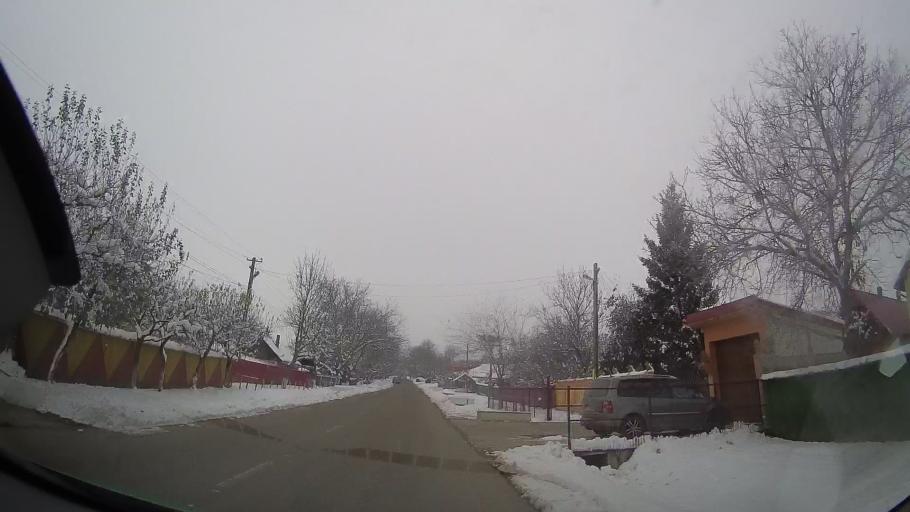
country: RO
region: Vaslui
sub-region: Comuna Bacesti
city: Bacesti
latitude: 46.8147
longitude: 27.2001
